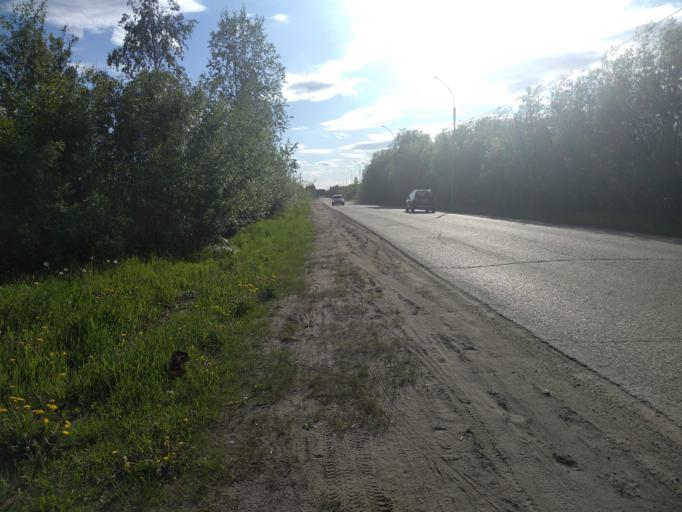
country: RU
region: Komi Republic
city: Pechora
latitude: 65.1377
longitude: 57.1592
